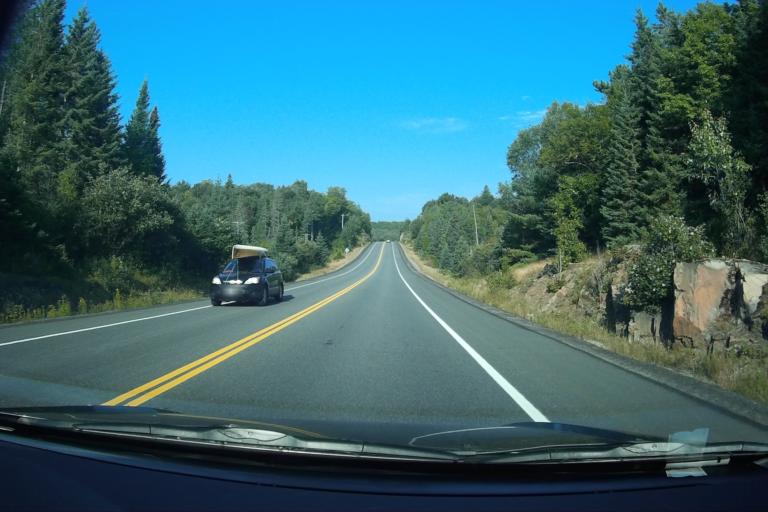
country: CA
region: Ontario
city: Huntsville
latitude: 45.5525
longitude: -78.6167
